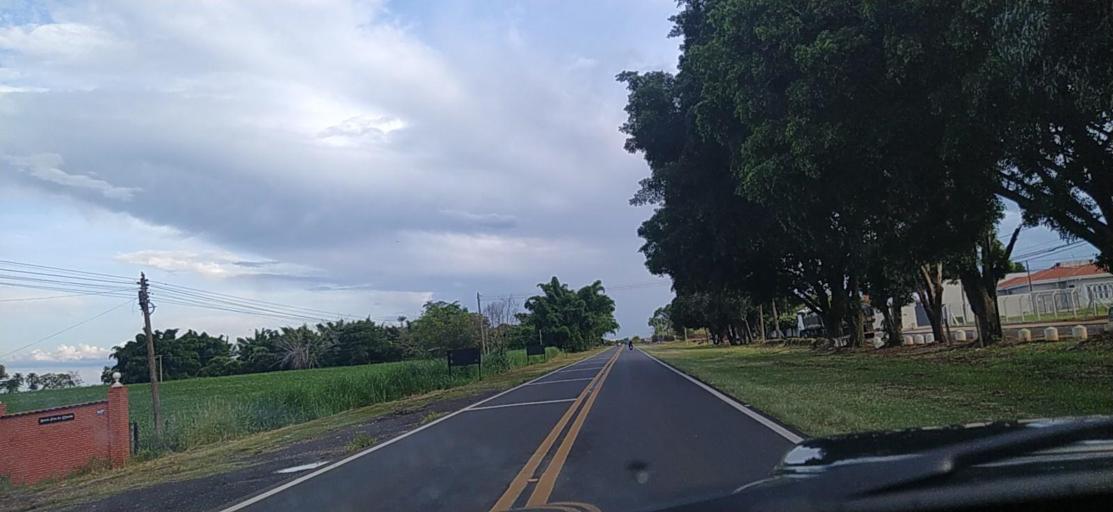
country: BR
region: Sao Paulo
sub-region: Pindorama
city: Pindorama
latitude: -21.1742
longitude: -48.9230
